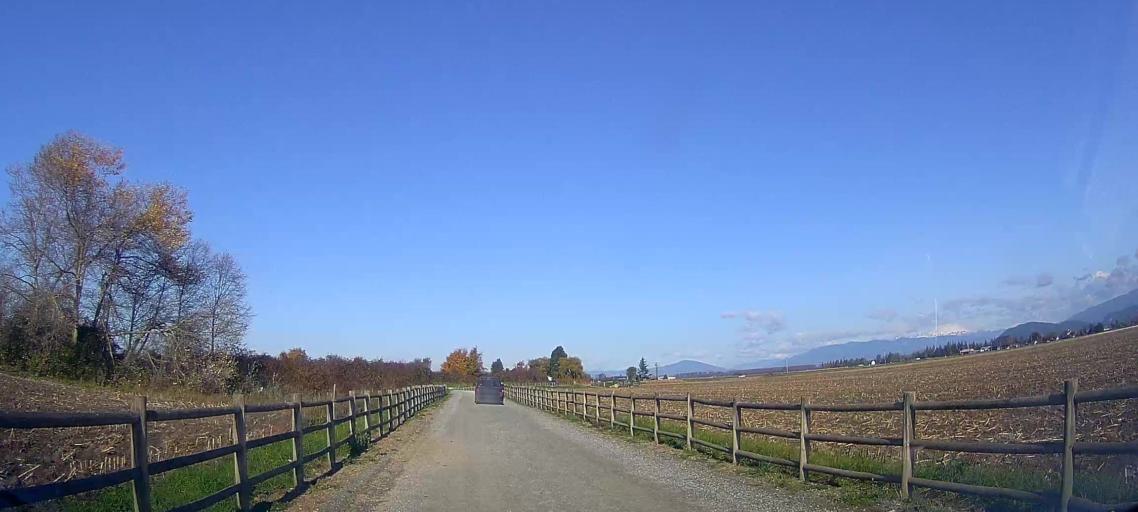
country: US
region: Washington
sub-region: Snohomish County
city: Stanwood
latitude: 48.3373
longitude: -122.4124
